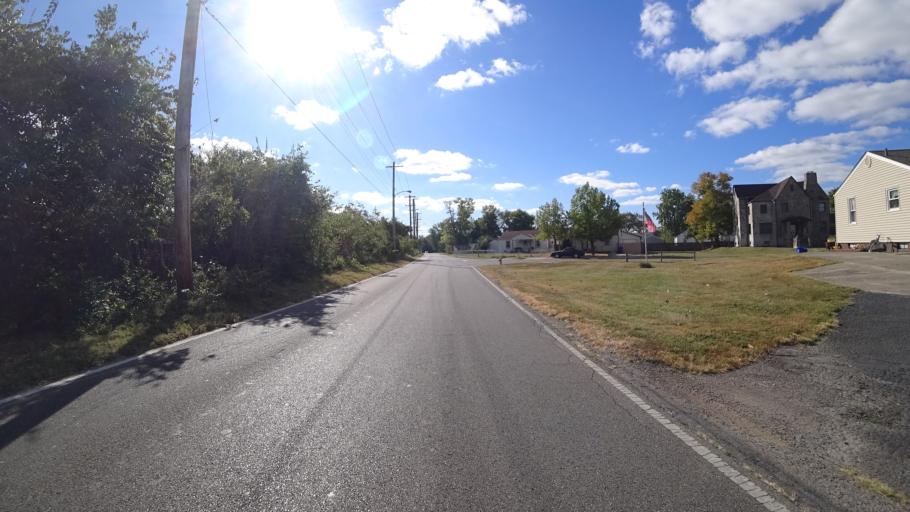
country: US
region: Ohio
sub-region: Butler County
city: Fairfield
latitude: 39.3654
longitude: -84.5484
